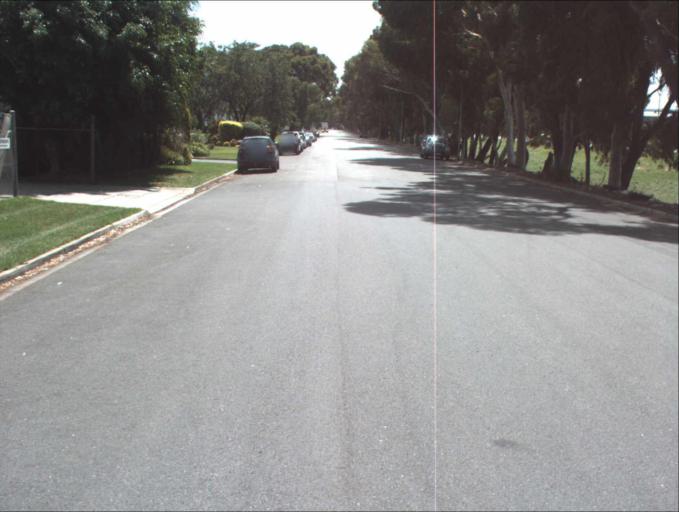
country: AU
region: South Australia
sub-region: Port Adelaide Enfield
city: Blair Athol
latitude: -34.8565
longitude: 138.5738
